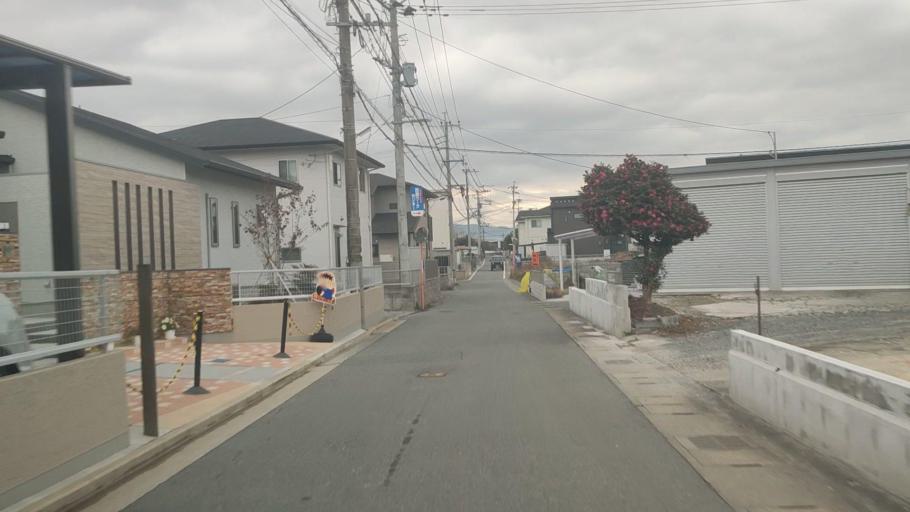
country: JP
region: Kumamoto
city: Ozu
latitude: 32.8291
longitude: 130.8000
